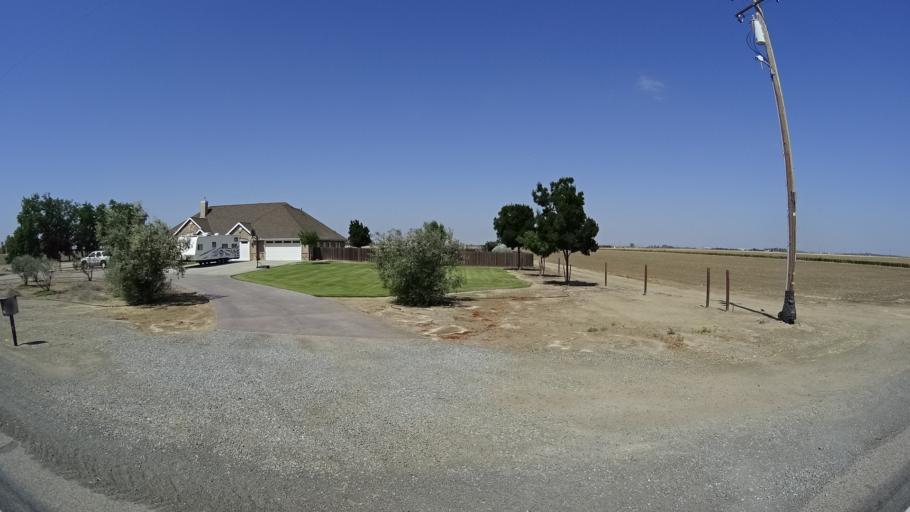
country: US
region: California
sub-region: Kings County
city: Home Garden
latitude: 36.2202
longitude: -119.6369
